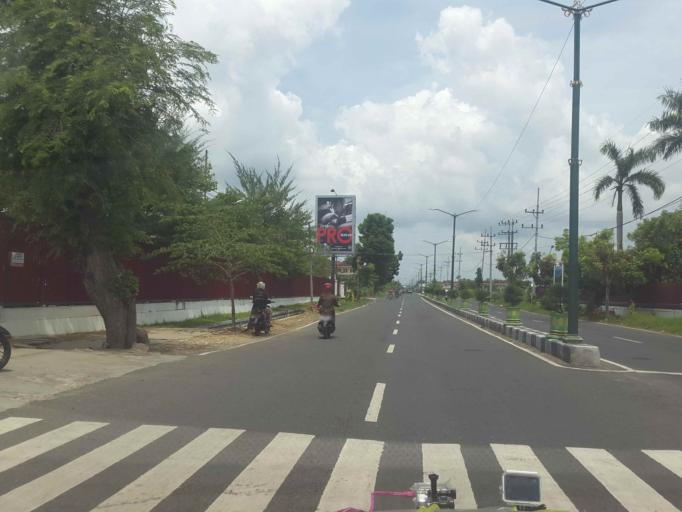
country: ID
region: East Java
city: Sumenep
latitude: -7.0397
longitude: 113.8483
